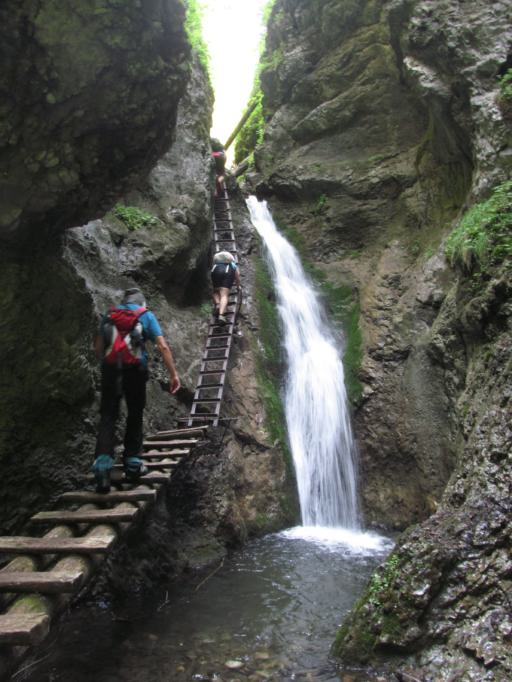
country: SK
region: Kosicky
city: Dobsina
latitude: 48.9148
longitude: 20.3695
